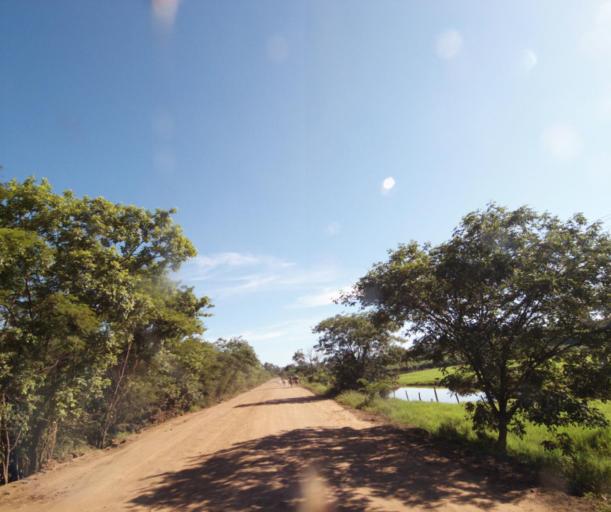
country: BR
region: Bahia
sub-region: Sao Felix Do Coribe
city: Santa Maria da Vitoria
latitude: -13.6438
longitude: -44.4408
